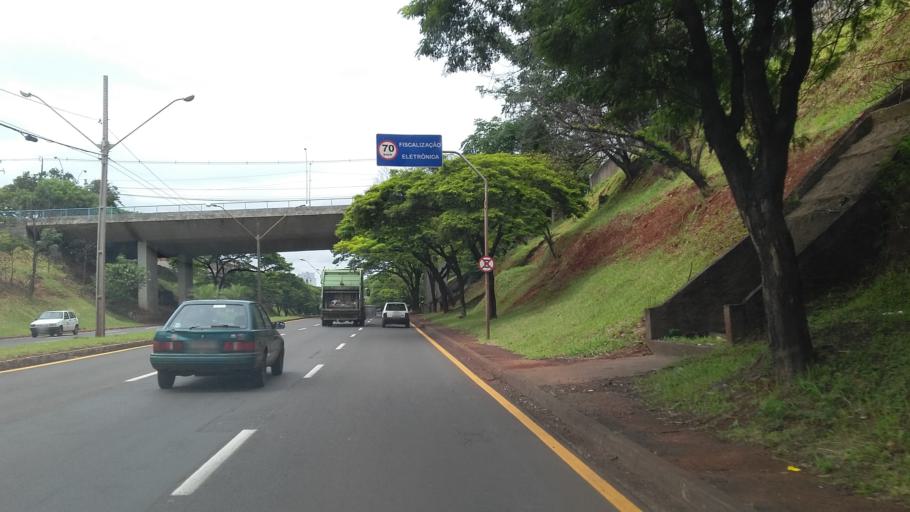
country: BR
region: Parana
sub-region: Londrina
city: Londrina
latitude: -23.3134
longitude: -51.1499
